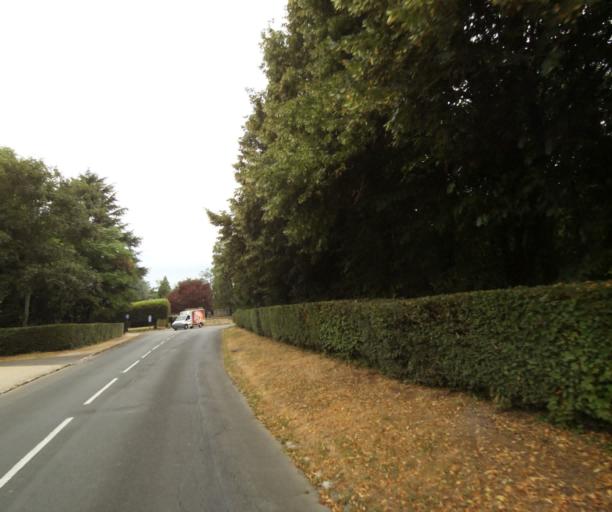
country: FR
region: Ile-de-France
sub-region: Departement de Seine-et-Marne
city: Cely
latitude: 48.4467
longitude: 2.5503
